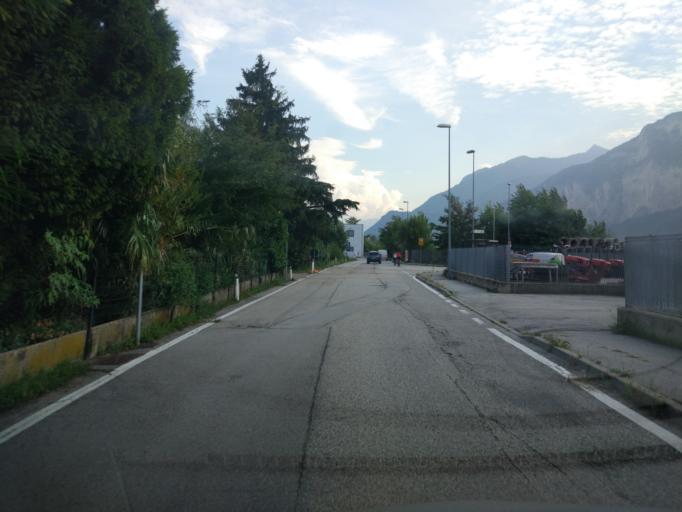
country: IT
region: Trentino-Alto Adige
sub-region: Provincia di Trento
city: Meano
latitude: 46.1174
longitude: 11.1008
